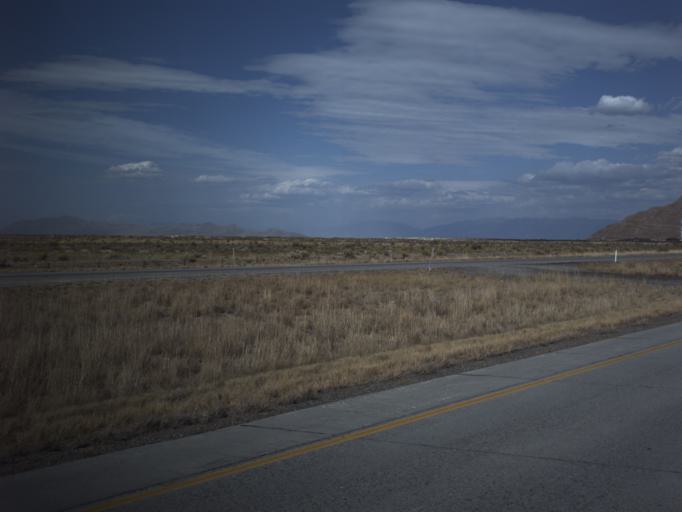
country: US
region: Utah
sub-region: Tooele County
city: Stansbury park
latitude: 40.6680
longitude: -112.3035
